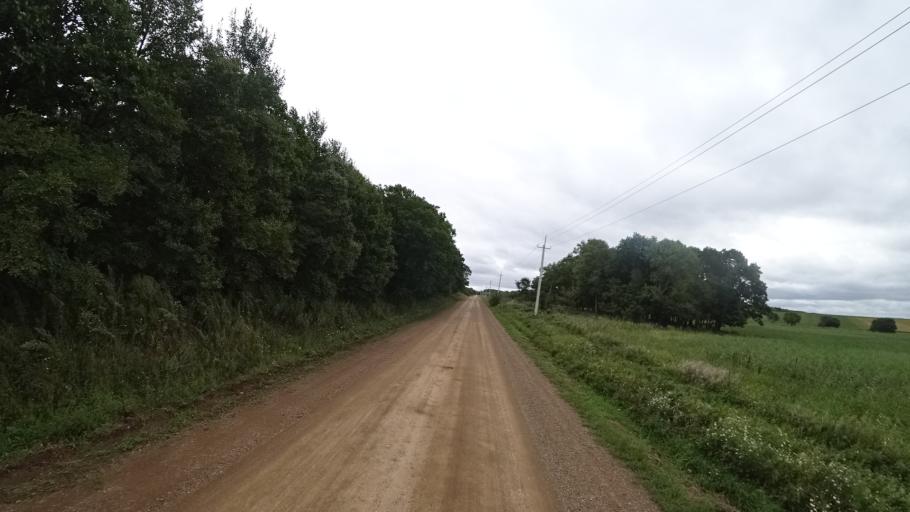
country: RU
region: Primorskiy
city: Chernigovka
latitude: 44.4688
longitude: 132.5843
